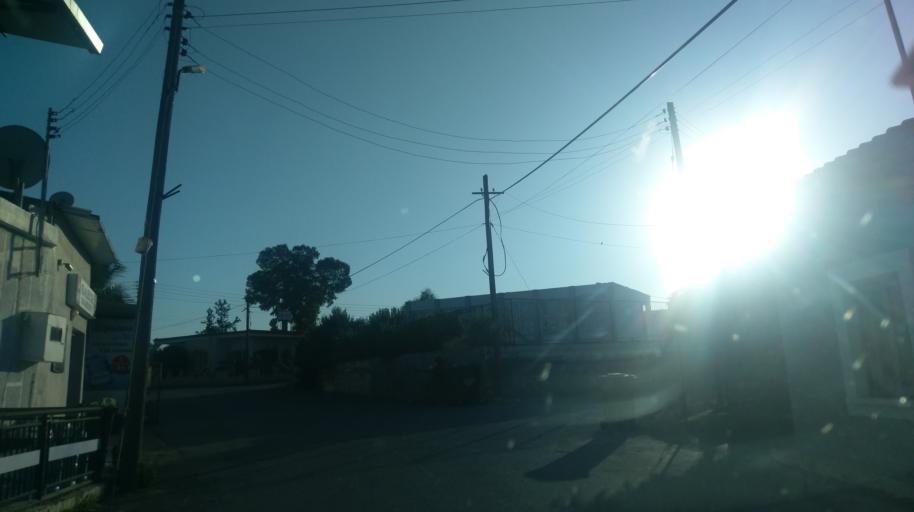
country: CY
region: Ammochostos
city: Lefkonoiko
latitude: 35.2245
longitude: 33.6178
